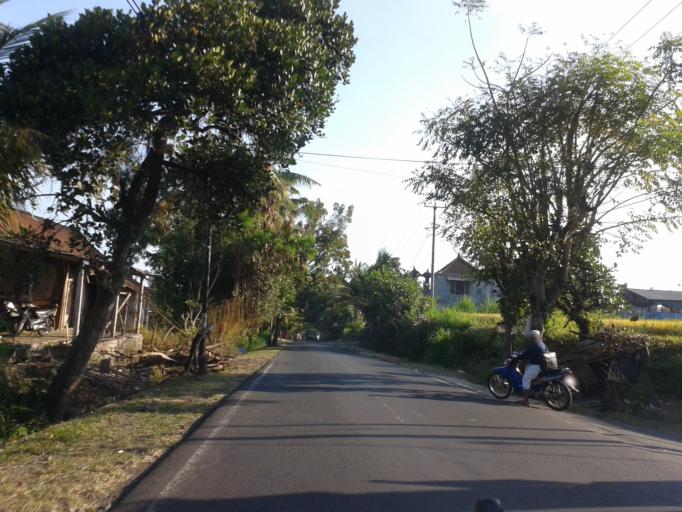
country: ID
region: Bali
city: Banjar Wangsian
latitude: -8.5081
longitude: 115.4026
